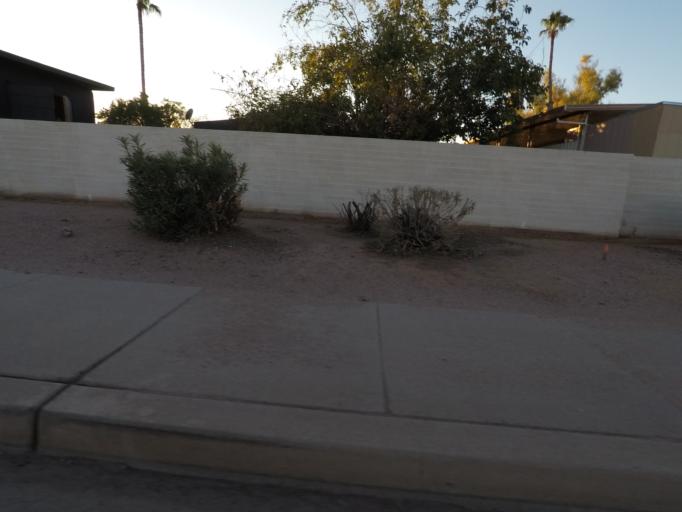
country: US
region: Arizona
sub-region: Maricopa County
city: Guadalupe
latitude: 33.3814
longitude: -111.9439
